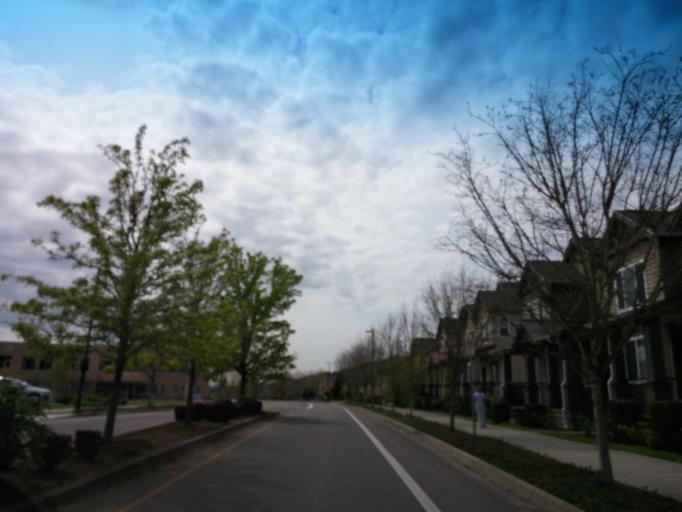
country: US
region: Oregon
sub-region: Washington County
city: Cedar Mill
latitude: 45.5254
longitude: -122.7981
